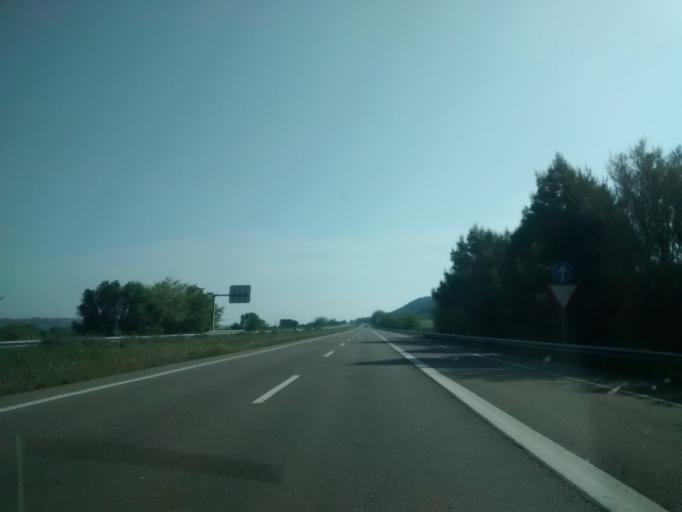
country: ES
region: Aragon
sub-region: Provincia de Huesca
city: Gurrea de Gallego
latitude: 41.9698
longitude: -0.7039
